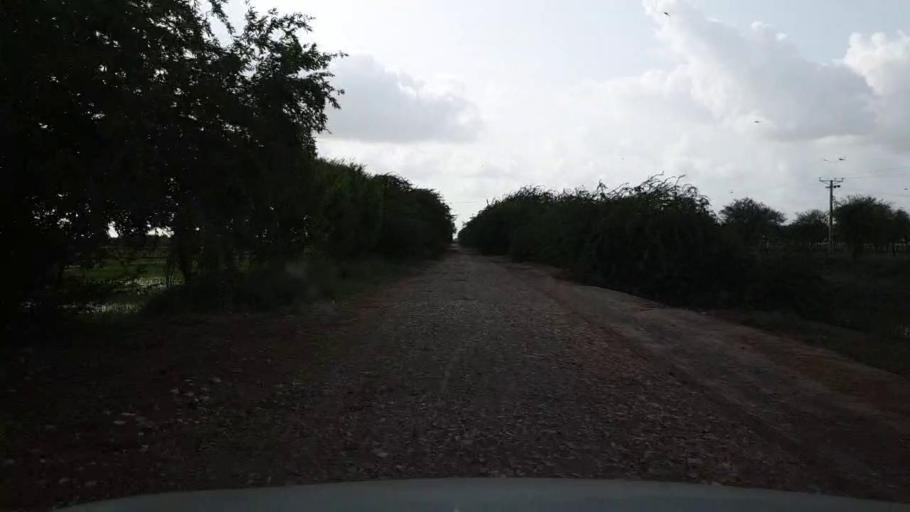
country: PK
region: Sindh
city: Kario
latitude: 24.7670
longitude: 68.5996
